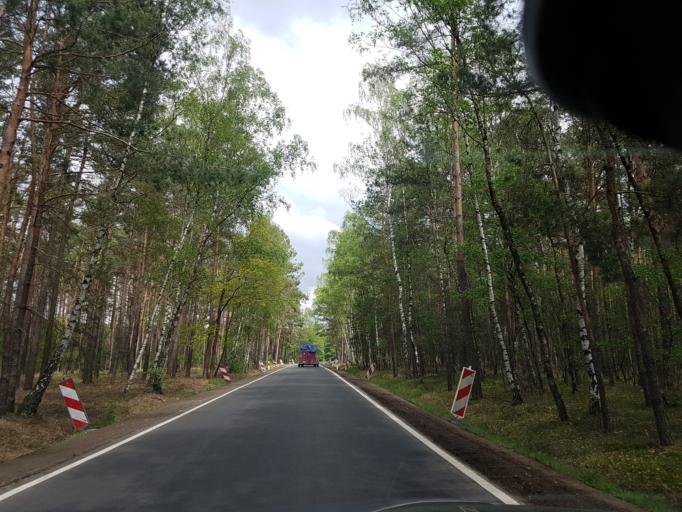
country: DE
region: Brandenburg
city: Finsterwalde
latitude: 51.6574
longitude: 13.7728
